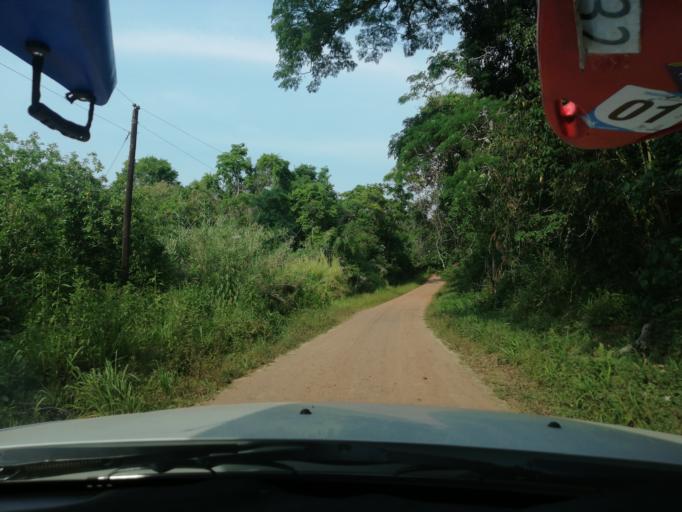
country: AR
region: Misiones
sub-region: Departamento de San Ignacio
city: San Ignacio
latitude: -27.3013
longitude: -55.5767
